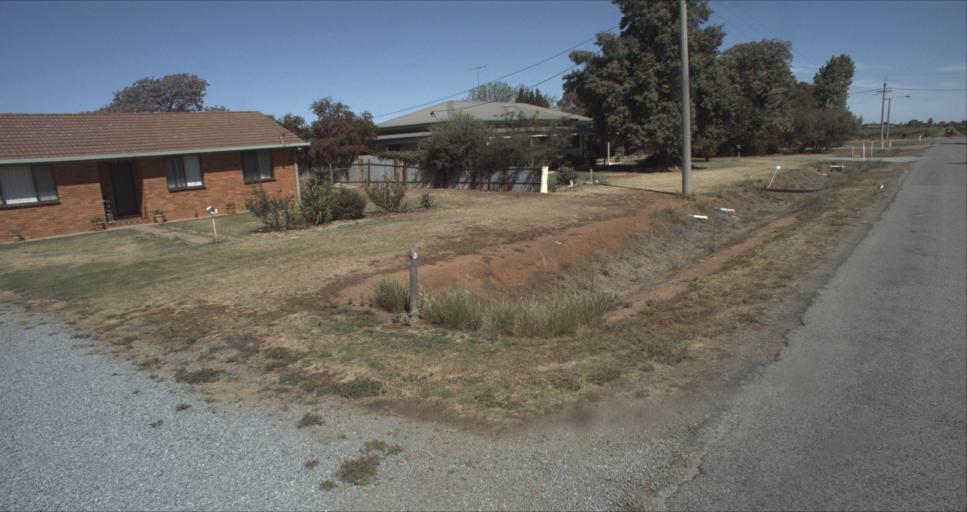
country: AU
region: New South Wales
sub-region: Leeton
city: Leeton
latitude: -34.5538
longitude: 146.3805
